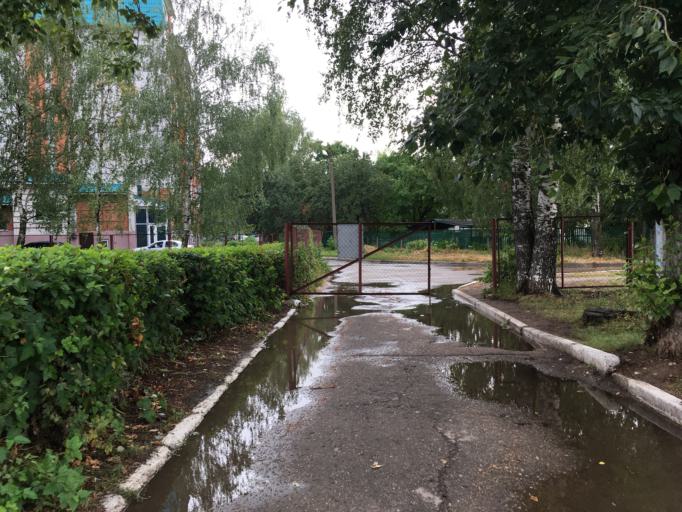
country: RU
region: Mariy-El
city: Yoshkar-Ola
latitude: 56.6490
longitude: 47.8692
